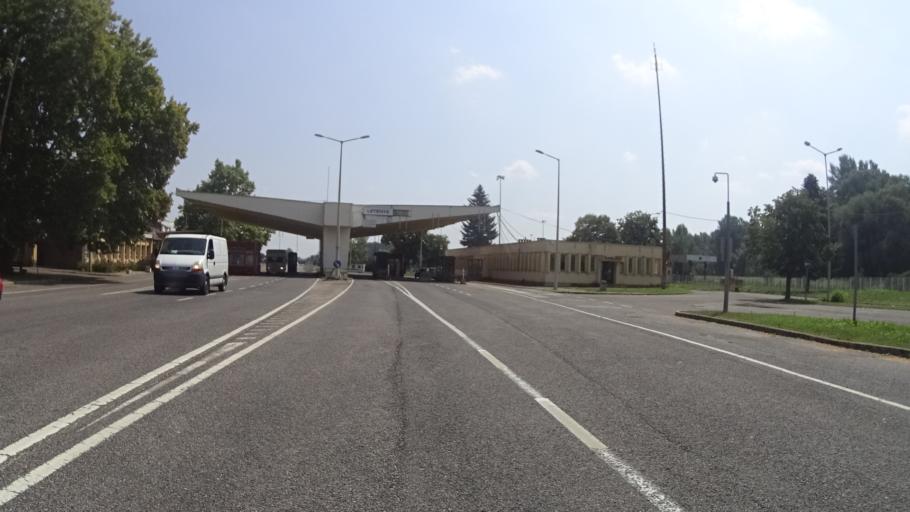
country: HU
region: Zala
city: Letenye
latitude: 46.4202
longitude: 16.6972
